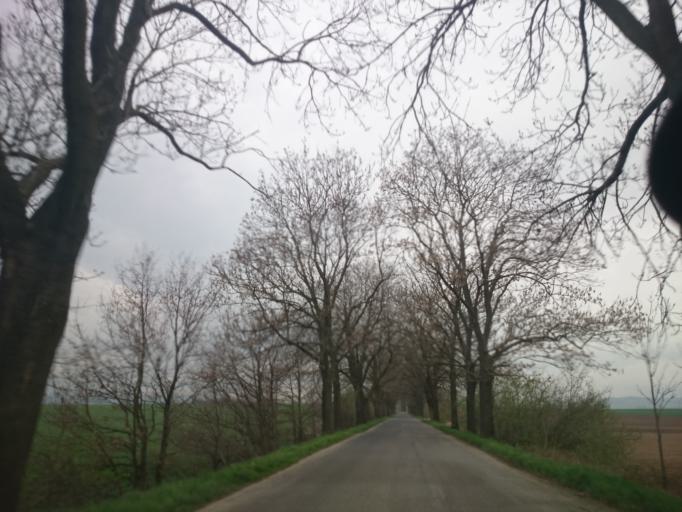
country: PL
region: Lower Silesian Voivodeship
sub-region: Powiat zabkowicki
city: Zabkowice Slaskie
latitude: 50.5610
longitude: 16.8426
